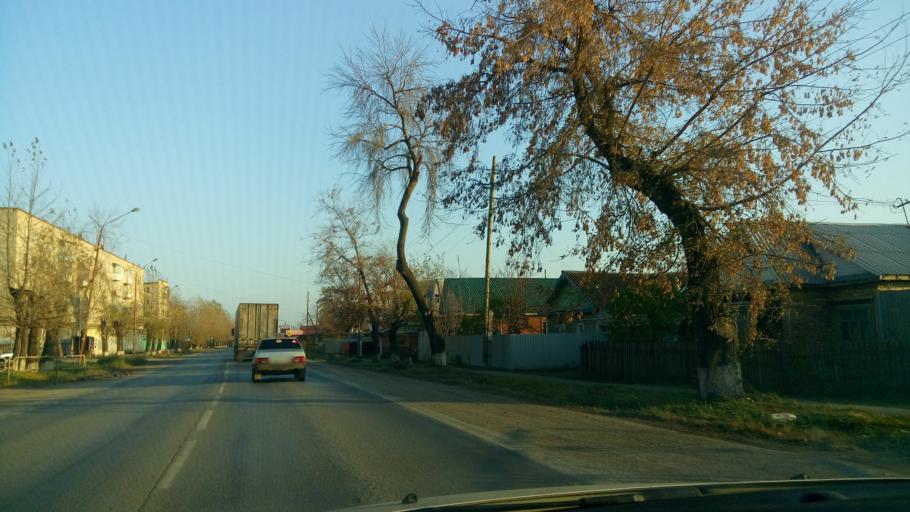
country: RU
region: Sverdlovsk
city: Bogdanovich
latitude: 56.7693
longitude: 62.0482
